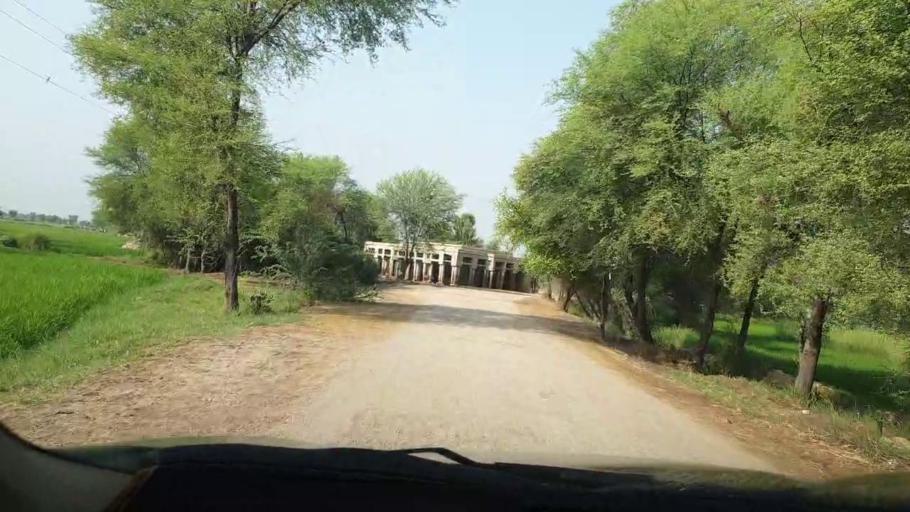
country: PK
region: Sindh
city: Goth Garelo
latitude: 27.4767
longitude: 68.0562
